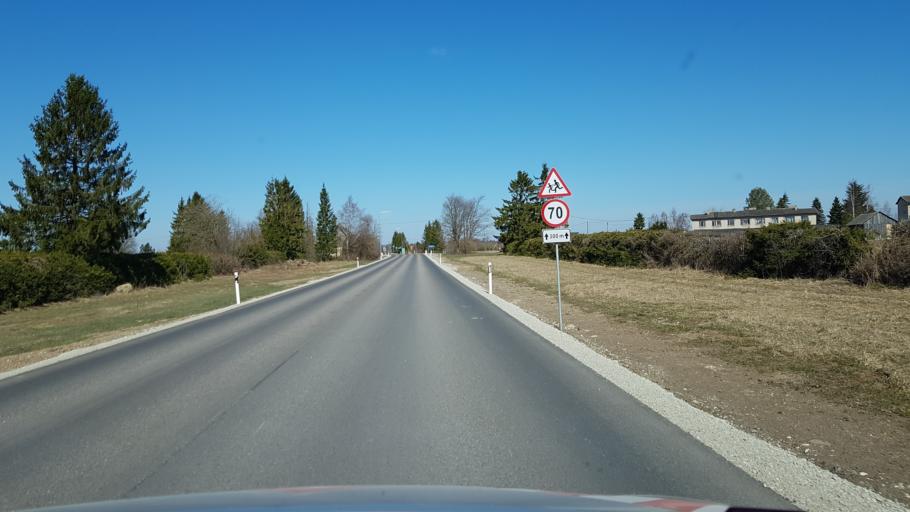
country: EE
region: Laeaene-Virumaa
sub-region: Vinni vald
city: Vinni
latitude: 59.0709
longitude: 26.6366
